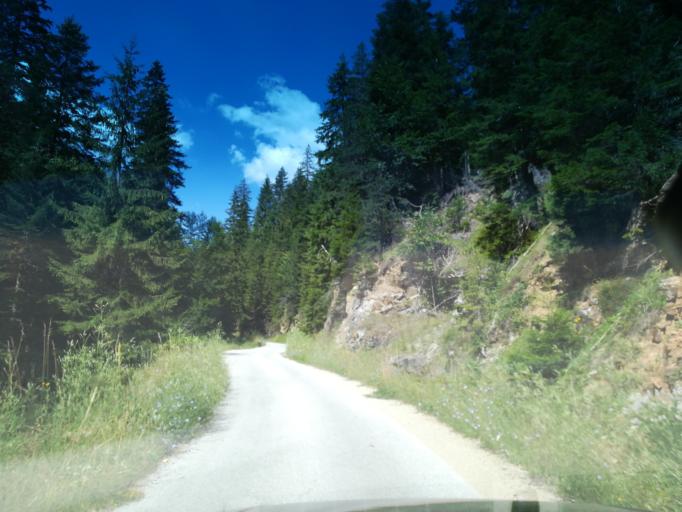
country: BG
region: Smolyan
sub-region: Obshtina Smolyan
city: Smolyan
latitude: 41.6602
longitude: 24.8114
